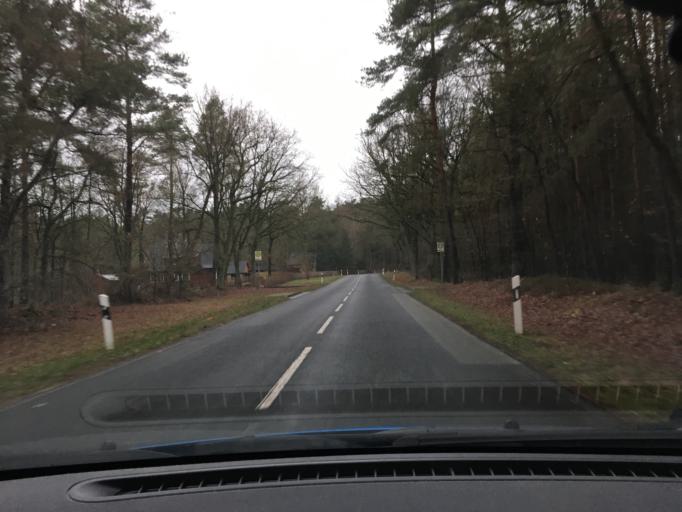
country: DE
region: Mecklenburg-Vorpommern
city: Nostorf
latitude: 53.4157
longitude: 10.6839
